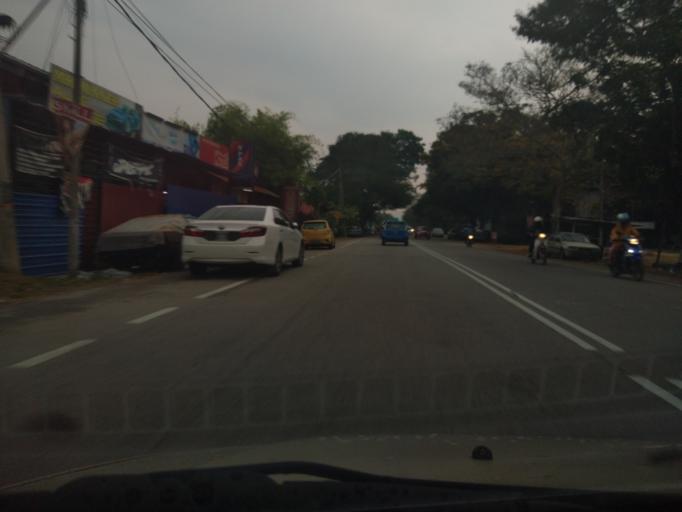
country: MY
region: Penang
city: Permatang Kuching
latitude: 5.4504
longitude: 100.4010
